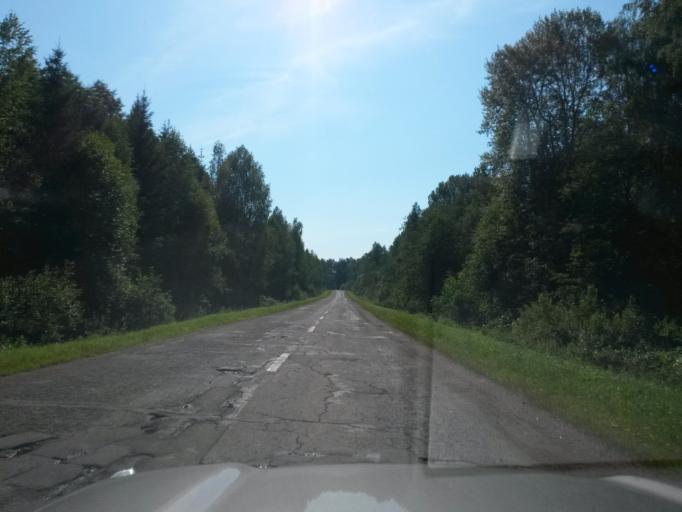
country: RU
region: Jaroslavl
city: Dubki
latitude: 57.2936
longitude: 40.0937
